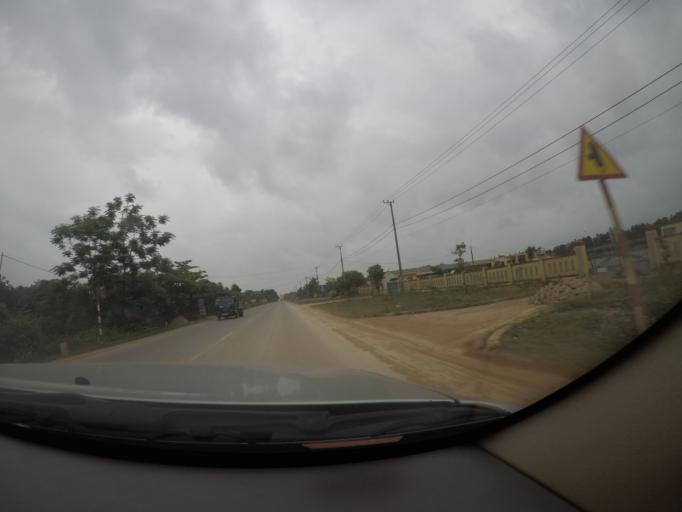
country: VN
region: Quang Tri
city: Dong Ha
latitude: 16.7902
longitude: 107.0834
